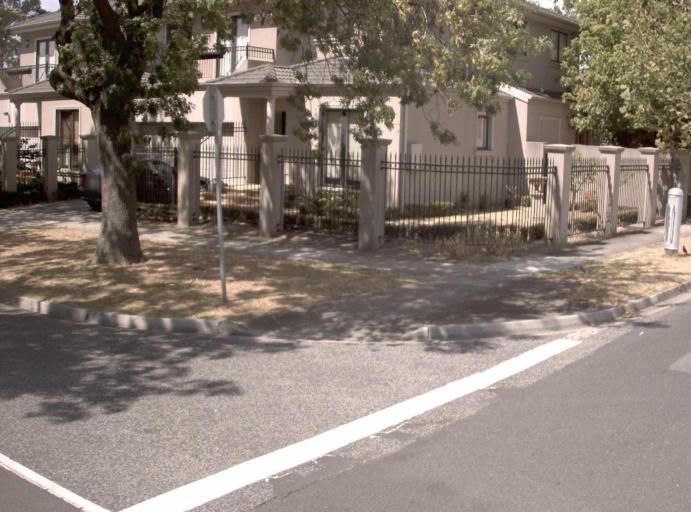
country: AU
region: Victoria
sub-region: Bayside
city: Brighton East
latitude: -37.9161
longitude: 145.0202
